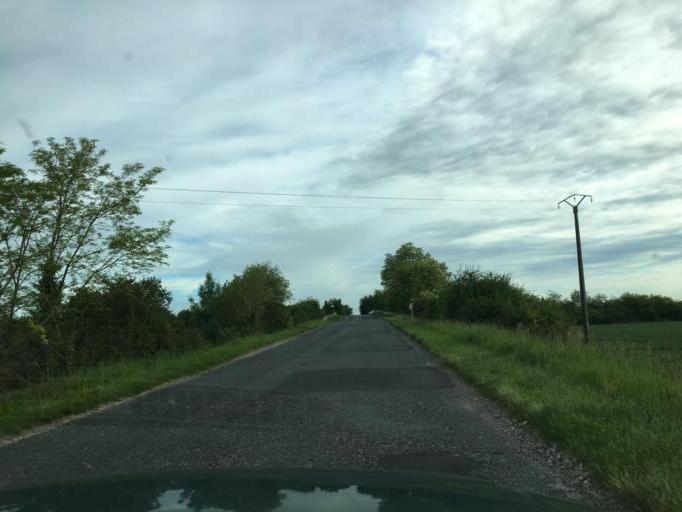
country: FR
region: Centre
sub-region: Departement du Loiret
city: La Chapelle-Saint-Mesmin
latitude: 47.8985
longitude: 1.8092
